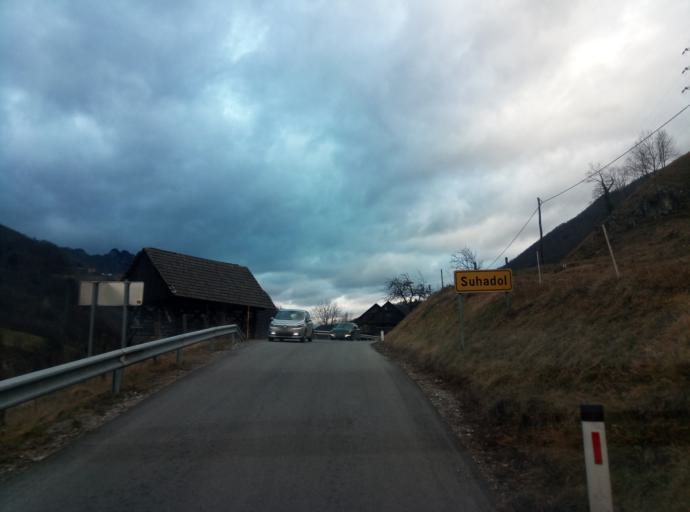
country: SI
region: Radece
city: Radece
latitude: 46.1000
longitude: 15.1470
